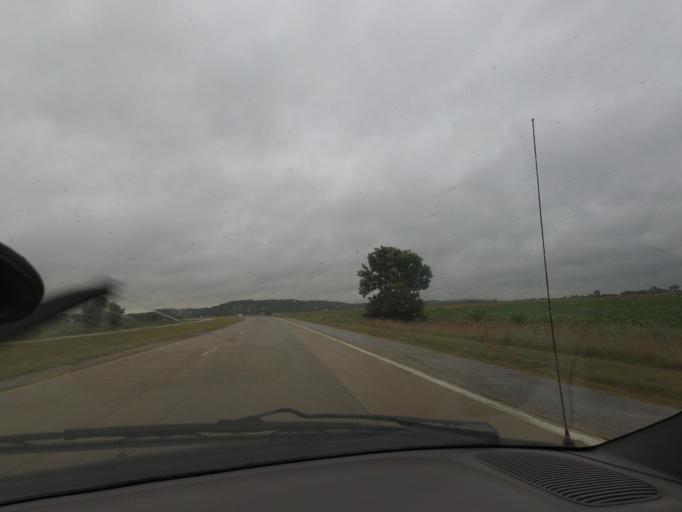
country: US
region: Illinois
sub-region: Adams County
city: Payson
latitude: 39.7178
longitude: -91.1881
